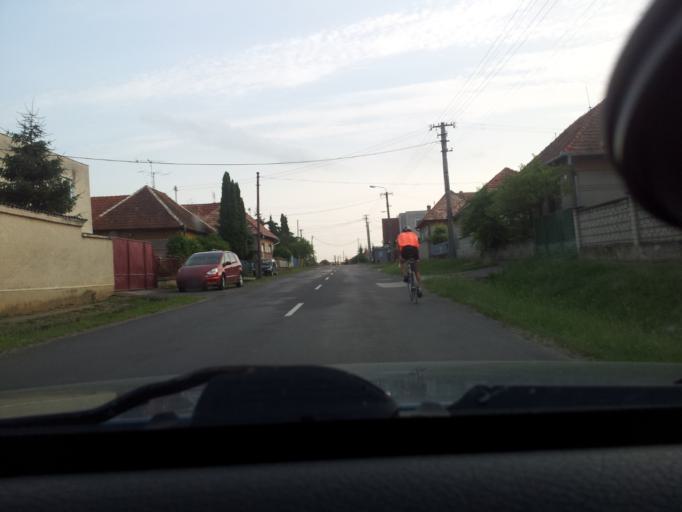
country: SK
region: Nitriansky
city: Levice
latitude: 48.2834
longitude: 18.6490
